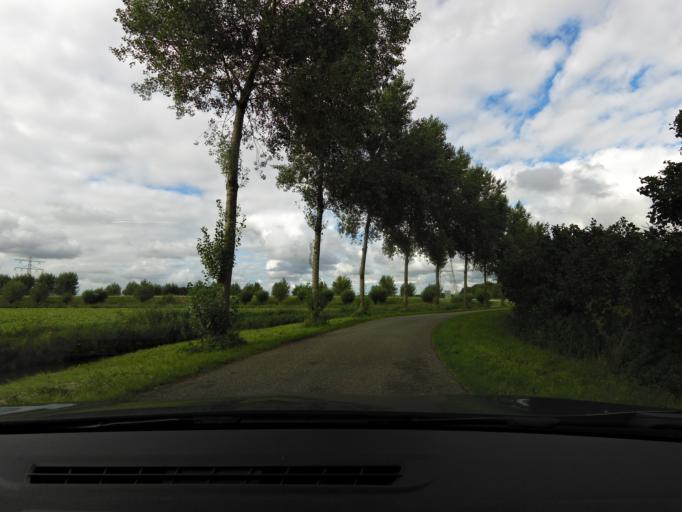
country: NL
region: South Holland
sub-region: Gemeente Brielle
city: Brielle
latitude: 51.8706
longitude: 4.2102
